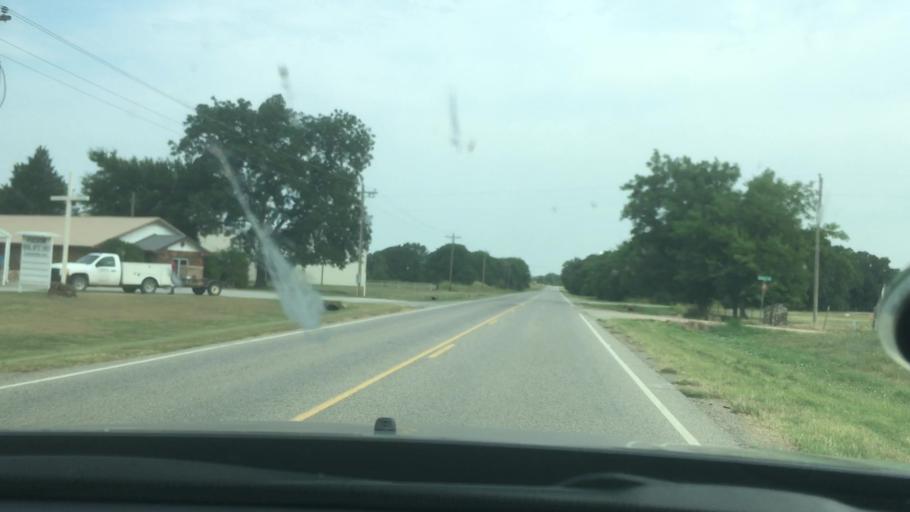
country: US
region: Oklahoma
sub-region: Bryan County
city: Durant
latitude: 34.1929
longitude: -96.4201
